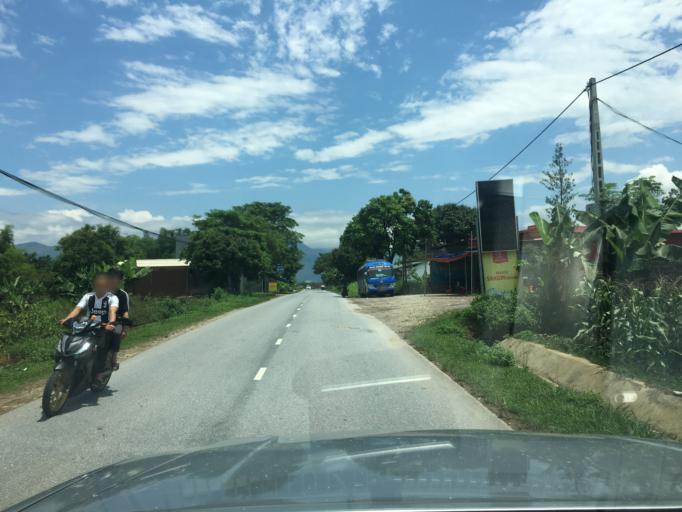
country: VN
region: Yen Bai
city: Son Thinh
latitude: 21.6244
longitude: 104.5093
